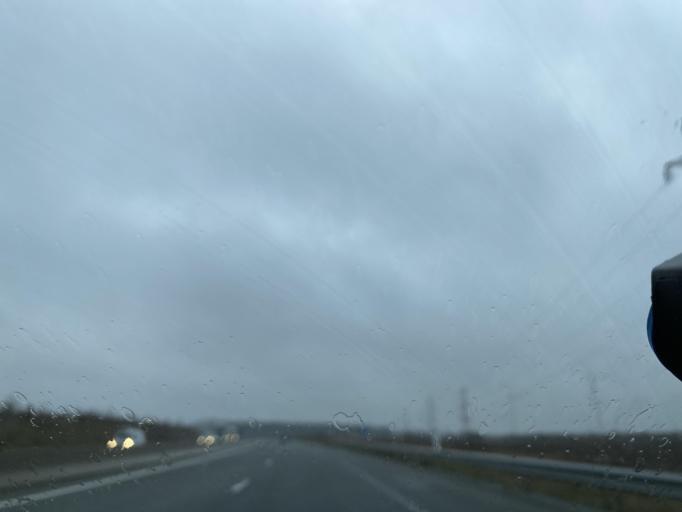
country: FR
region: Centre
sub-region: Departement d'Eure-et-Loir
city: Voves
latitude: 48.3290
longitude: 1.6506
